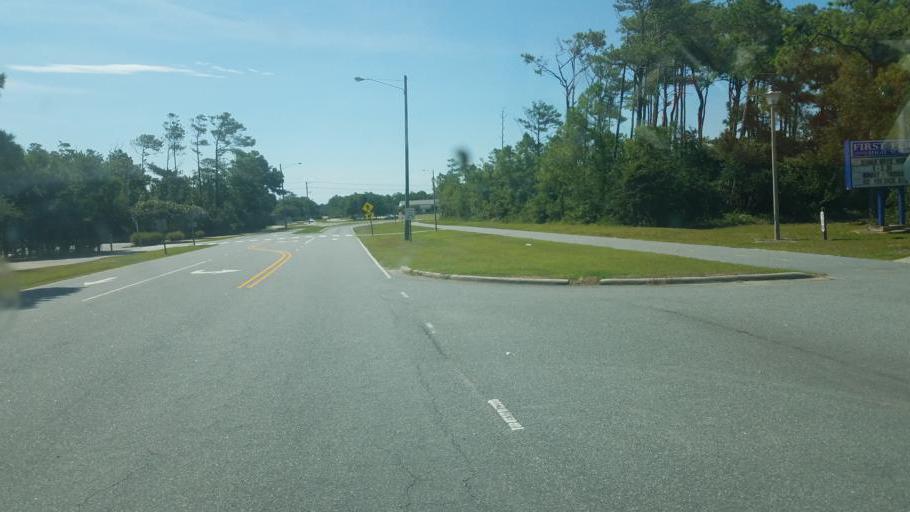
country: US
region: North Carolina
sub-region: Dare County
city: Kill Devil Hills
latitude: 36.0097
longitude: -75.6650
